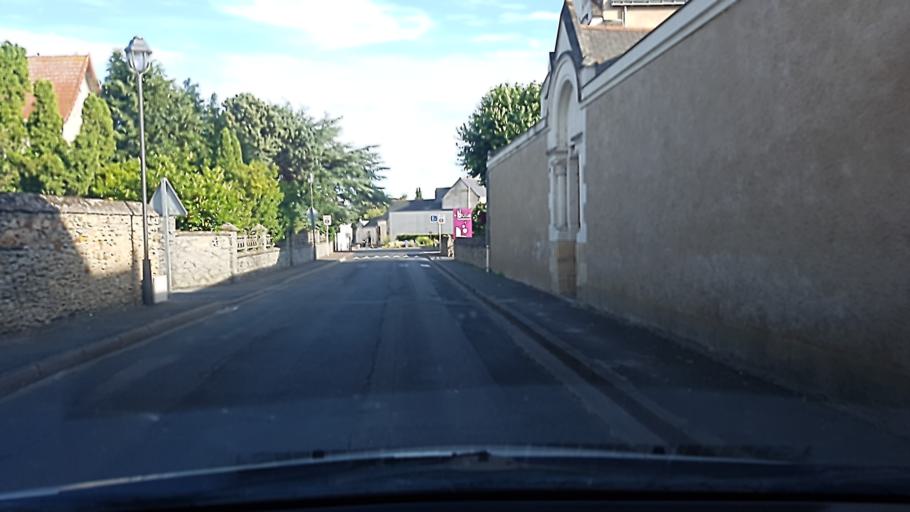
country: FR
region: Pays de la Loire
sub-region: Departement de Maine-et-Loire
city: Maze
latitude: 47.4579
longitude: -0.2723
